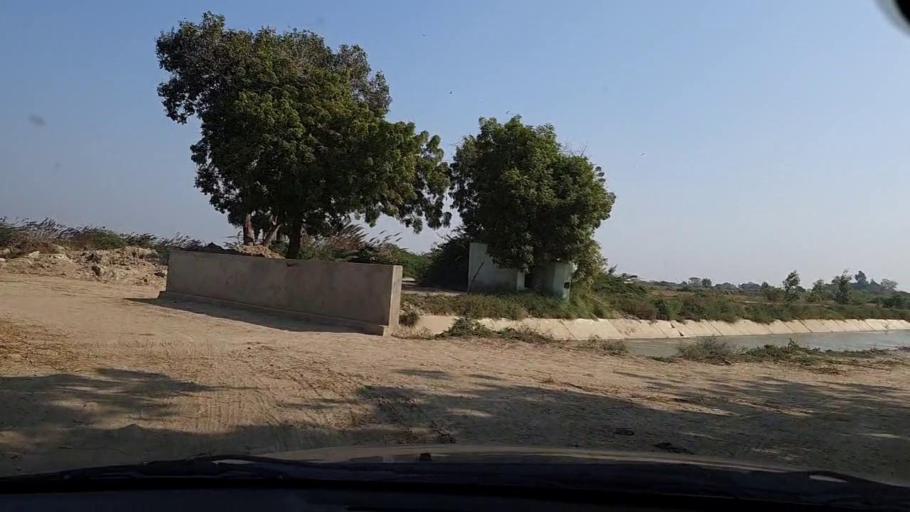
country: PK
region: Sindh
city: Mirpur Sakro
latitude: 24.3420
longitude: 67.7340
